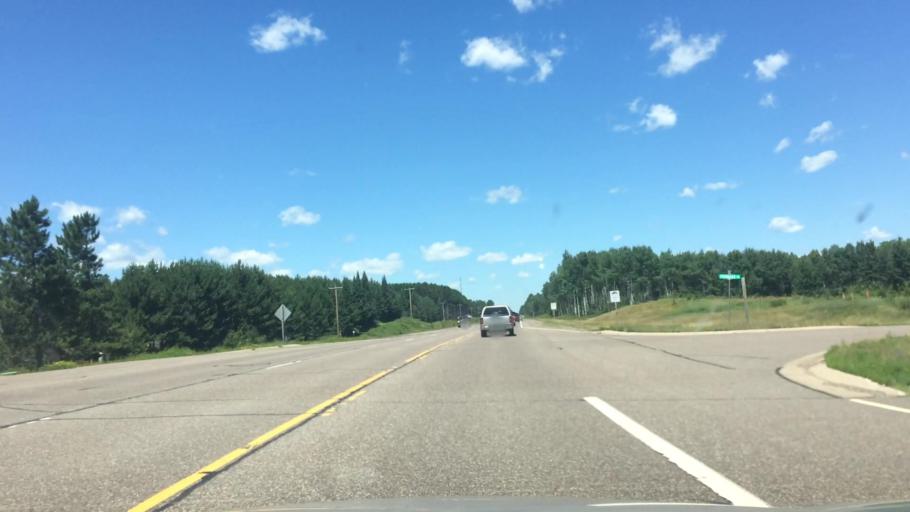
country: US
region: Wisconsin
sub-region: Lincoln County
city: Tomahawk
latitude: 45.6661
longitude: -89.7139
